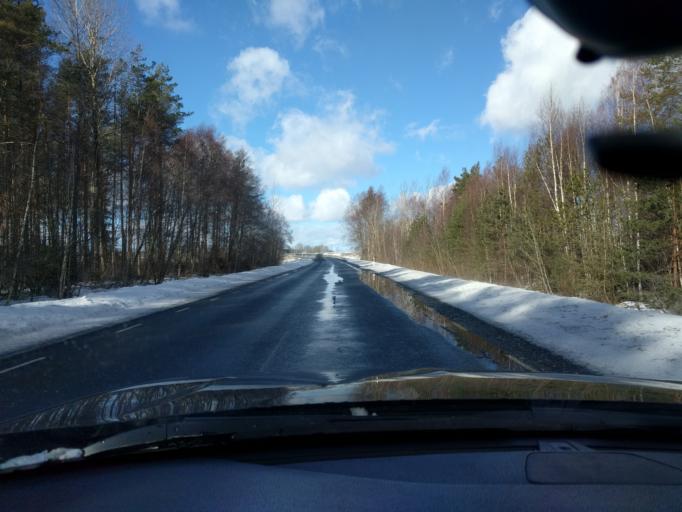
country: EE
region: Harju
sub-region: Anija vald
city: Kehra
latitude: 59.2401
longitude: 25.3701
